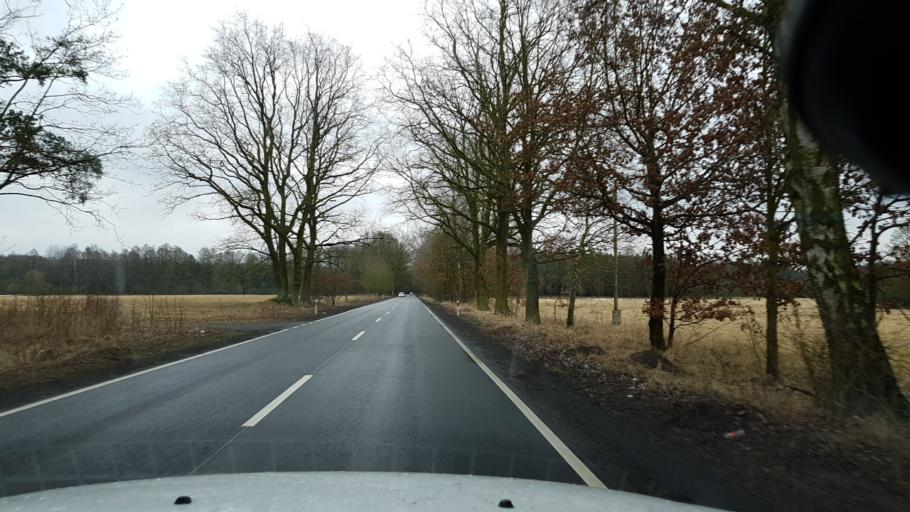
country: PL
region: West Pomeranian Voivodeship
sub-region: Powiat goleniowski
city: Stepnica
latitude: 53.6459
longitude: 14.6558
